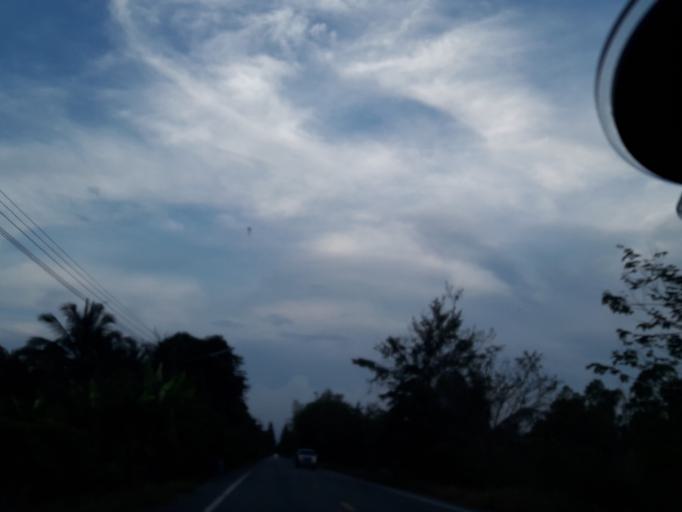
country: TH
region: Pathum Thani
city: Nong Suea
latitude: 14.1759
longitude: 100.8689
